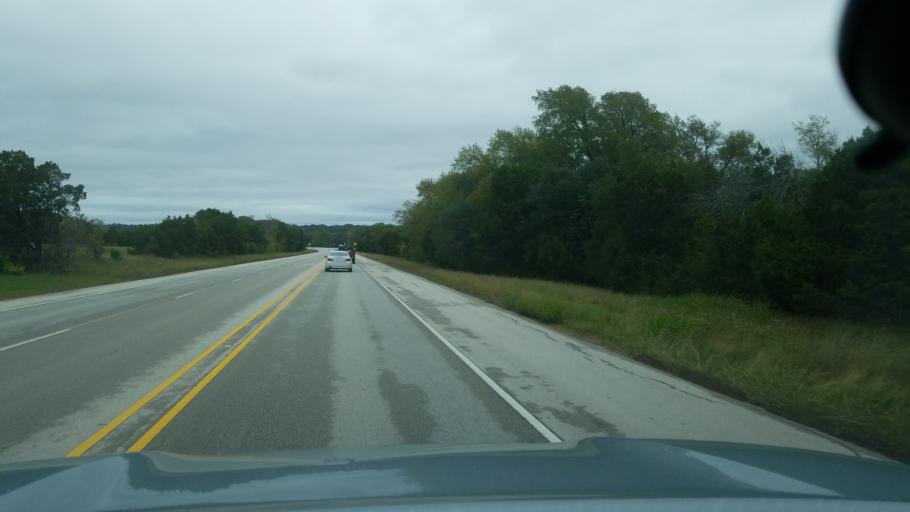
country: US
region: Texas
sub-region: Blanco County
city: Blanco
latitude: 29.9937
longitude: -98.4068
